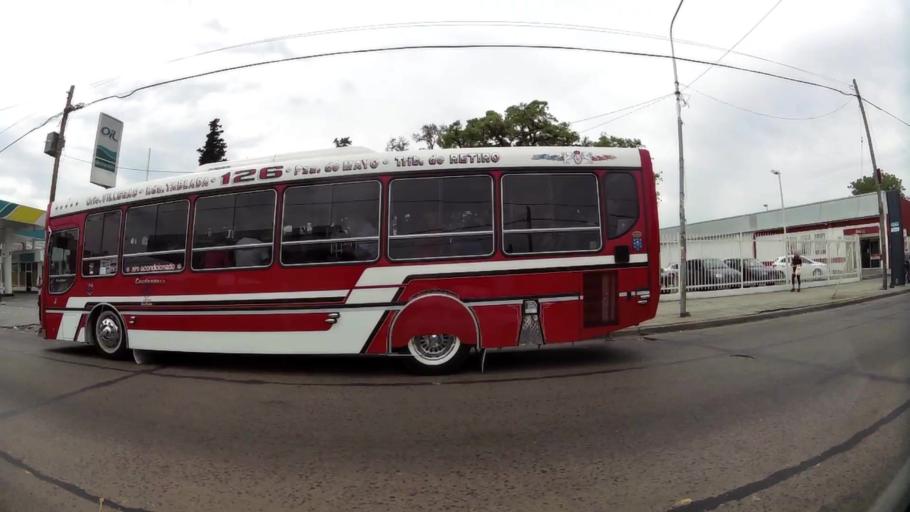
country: AR
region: Buenos Aires
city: San Justo
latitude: -34.6878
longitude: -58.5226
